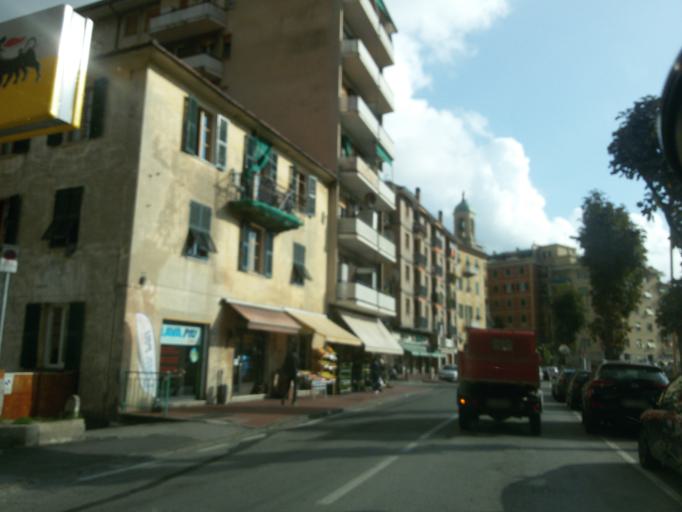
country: IT
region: Liguria
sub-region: Provincia di Genova
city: Recco
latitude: 44.3655
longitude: 9.1468
